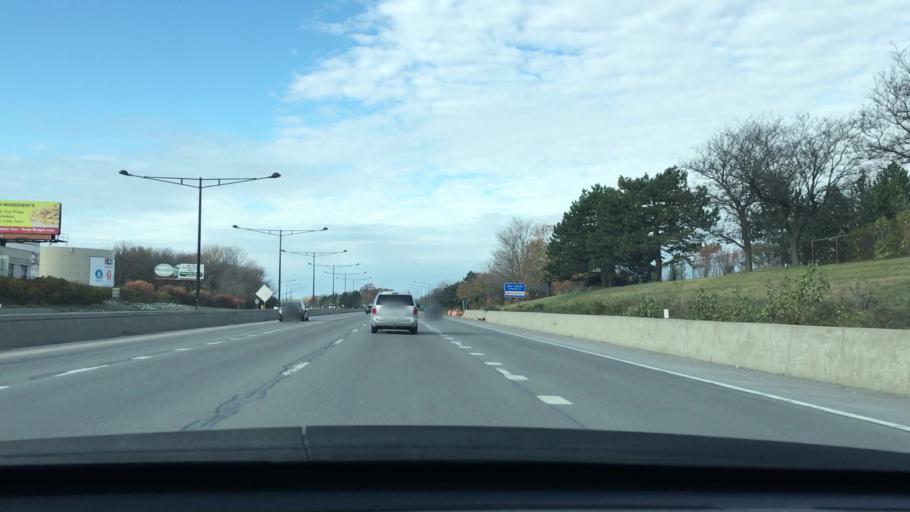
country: US
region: New York
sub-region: Monroe County
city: North Gates
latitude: 43.1577
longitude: -77.6662
